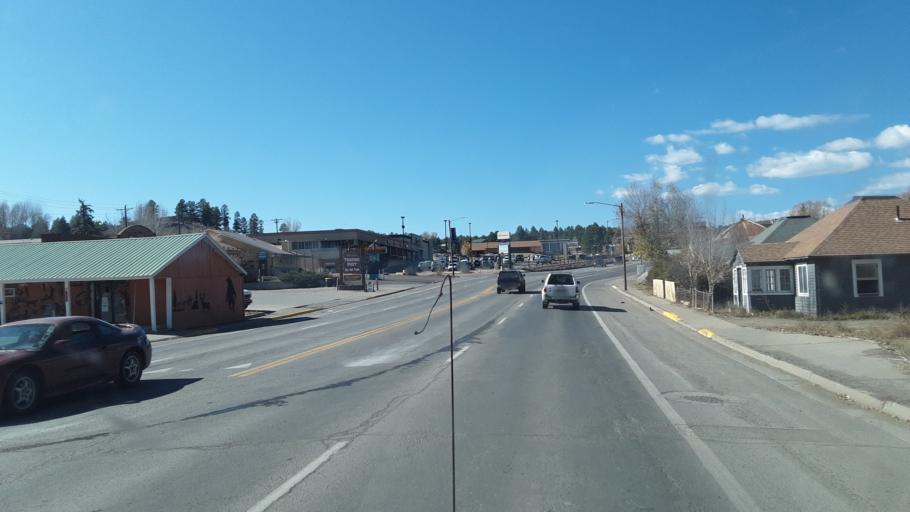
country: US
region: Colorado
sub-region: Archuleta County
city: Pagosa Springs
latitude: 37.2664
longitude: -107.0143
